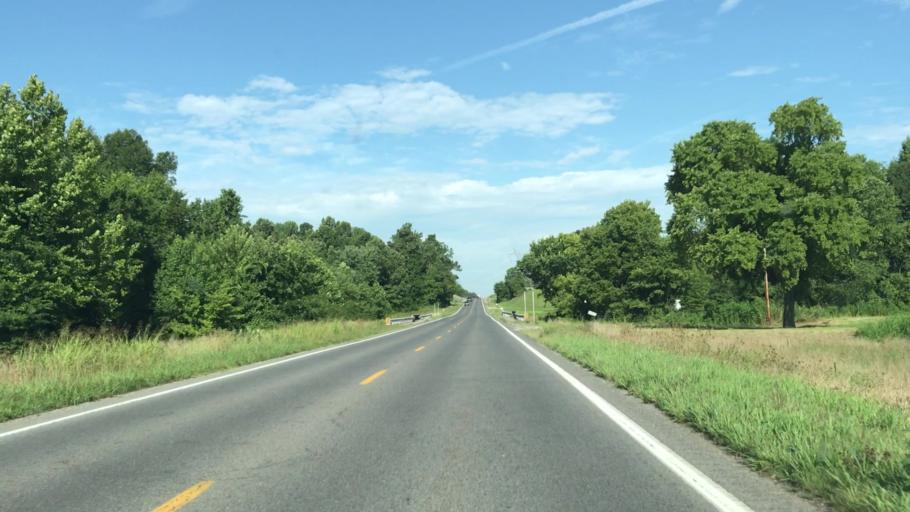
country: US
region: Kentucky
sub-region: Marshall County
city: Calvert City
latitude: 37.0054
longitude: -88.4096
